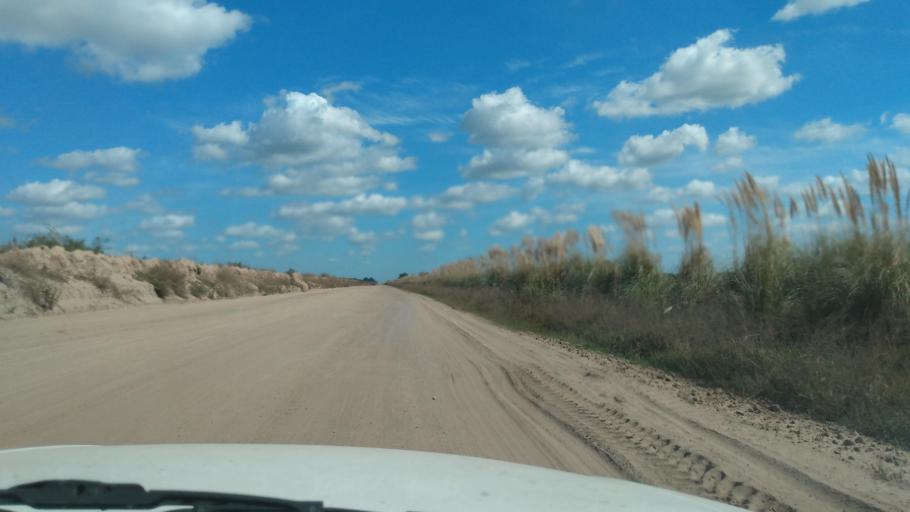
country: AR
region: Buenos Aires
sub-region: Partido de Navarro
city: Navarro
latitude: -35.0030
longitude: -59.3618
